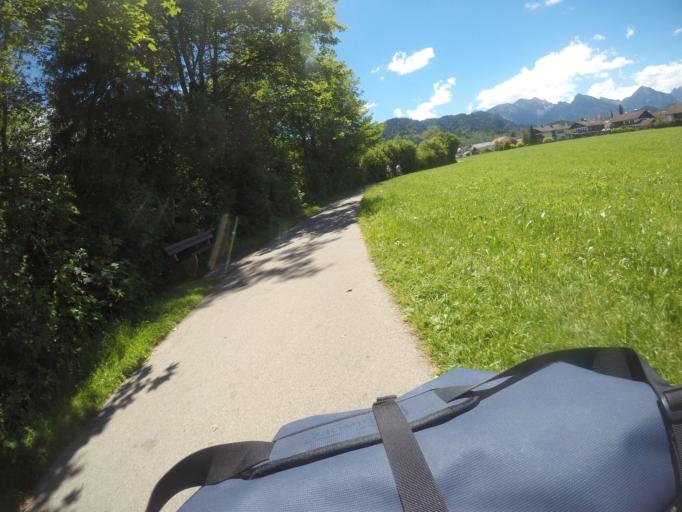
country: DE
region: Bavaria
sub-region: Swabia
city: Fuessen
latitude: 47.5736
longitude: 10.7119
